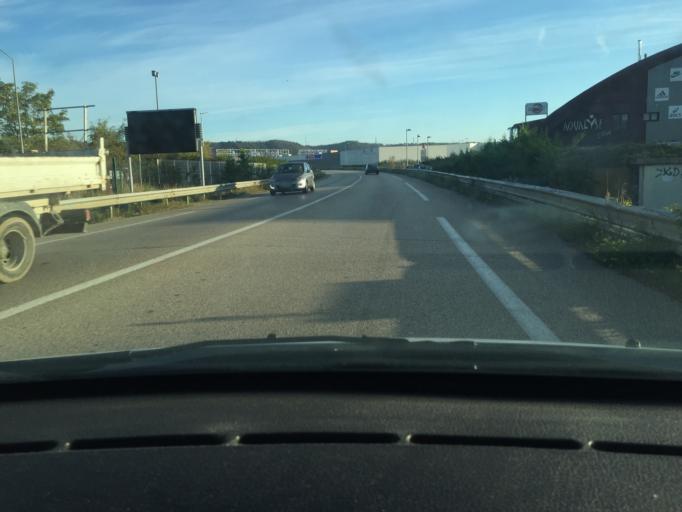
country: FR
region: Rhone-Alpes
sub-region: Departement de l'Ain
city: Saint-Maurice-de-Beynost
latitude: 45.8228
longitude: 4.9932
